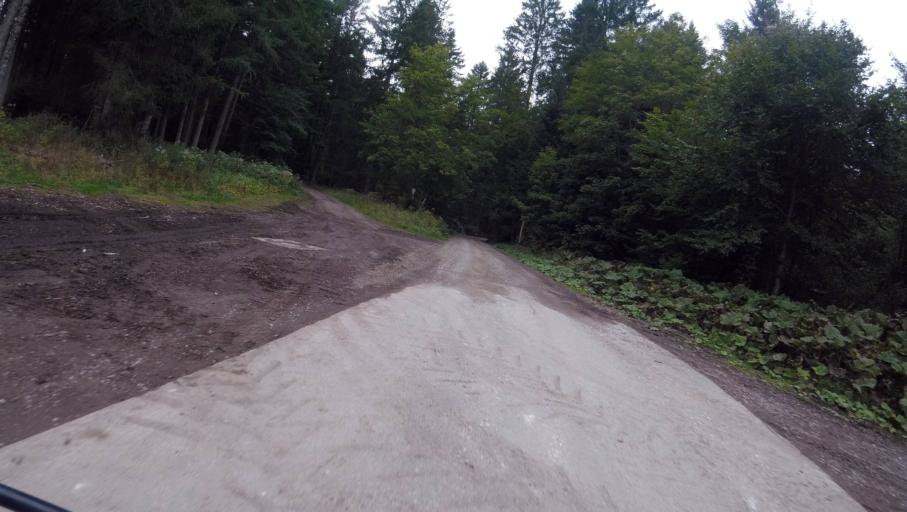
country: DE
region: Baden-Wuerttemberg
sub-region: Karlsruhe Region
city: Enzklosterle
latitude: 48.6044
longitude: 8.4367
